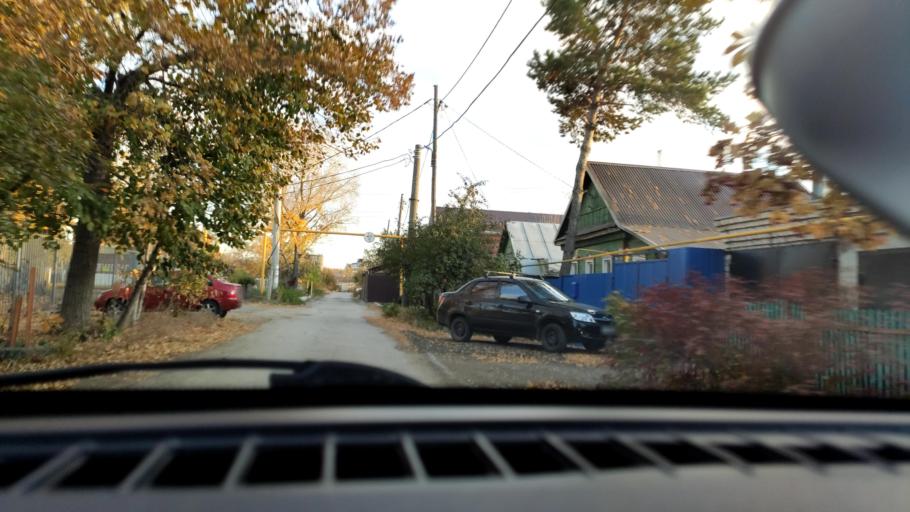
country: RU
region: Samara
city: Smyshlyayevka
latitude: 53.2303
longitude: 50.3054
